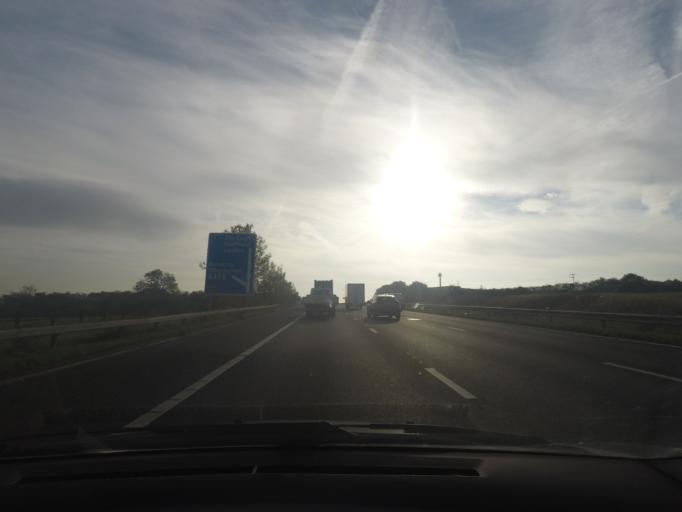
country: GB
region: England
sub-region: Barnsley
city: Dodworth
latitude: 53.5546
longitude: -1.5256
